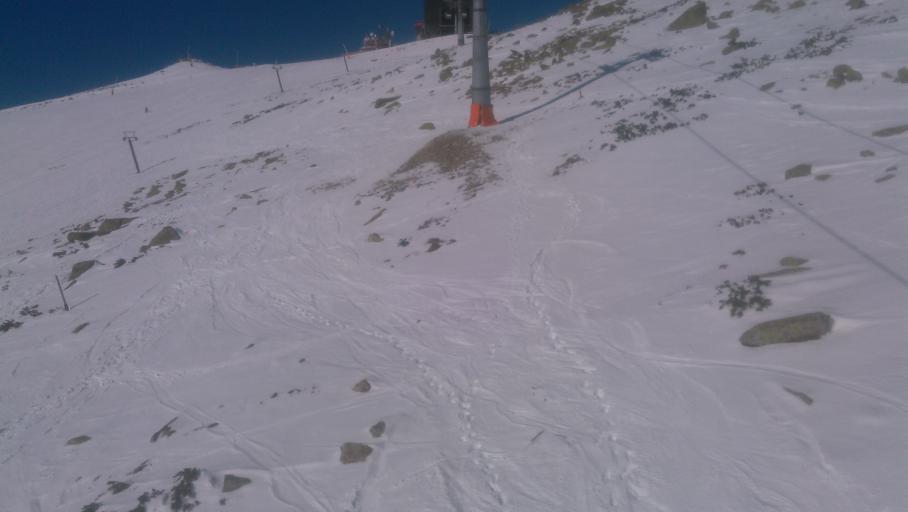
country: SK
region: Banskobystricky
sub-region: Okres Banska Bystrica
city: Brezno
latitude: 48.9406
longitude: 19.5925
